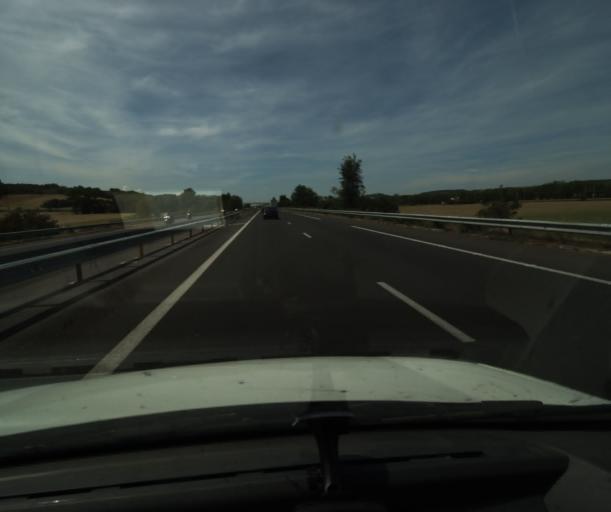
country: FR
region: Midi-Pyrenees
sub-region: Departement de la Haute-Garonne
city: Avignonet-Lauragais
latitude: 43.3298
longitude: 1.8480
